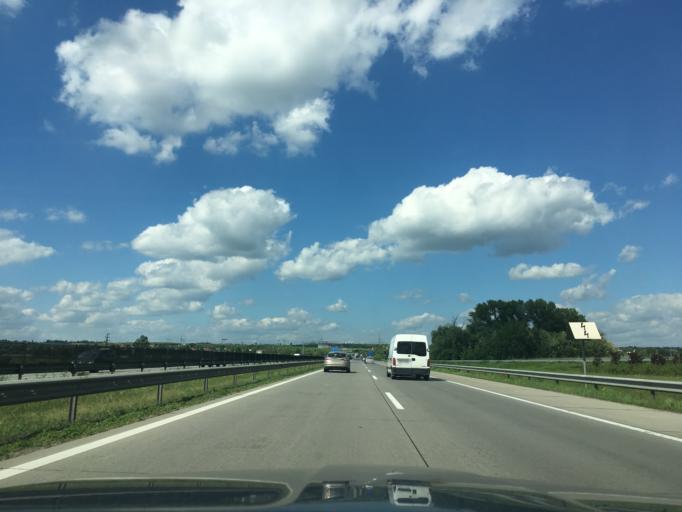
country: HU
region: Pest
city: Ecser
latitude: 47.4318
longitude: 19.3272
